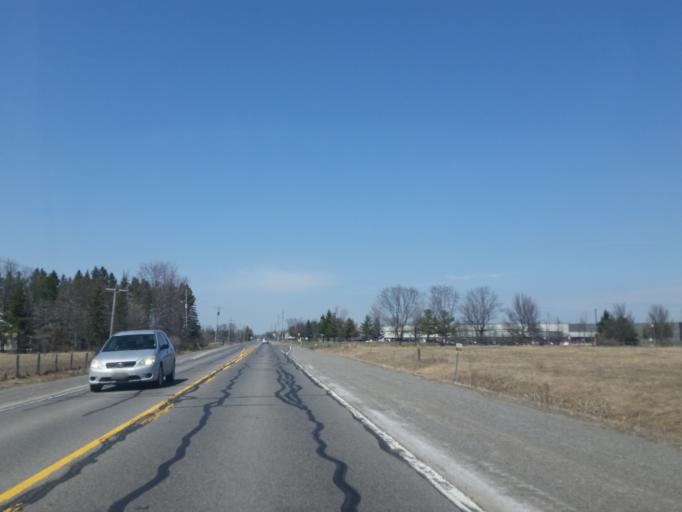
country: CA
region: Ontario
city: Bells Corners
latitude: 45.4312
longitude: -76.0325
